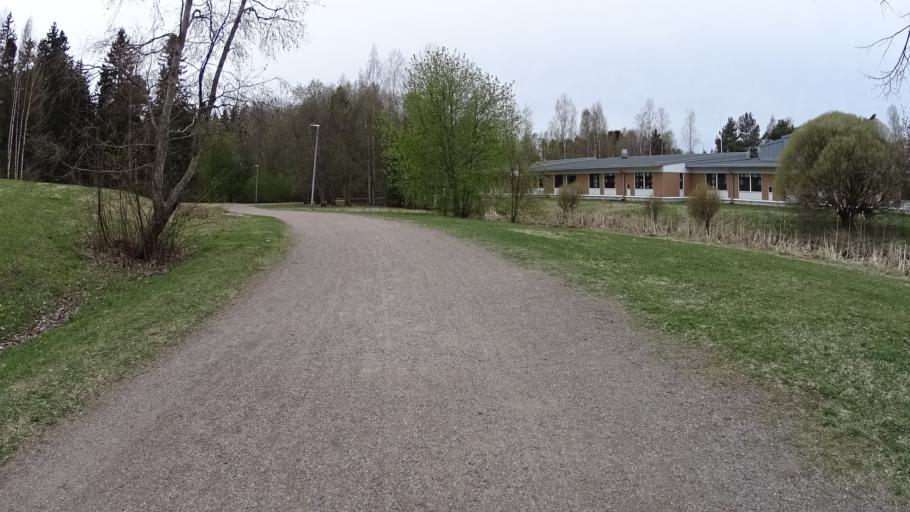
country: FI
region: Uusimaa
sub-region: Helsinki
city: Kilo
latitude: 60.2723
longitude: 24.8175
